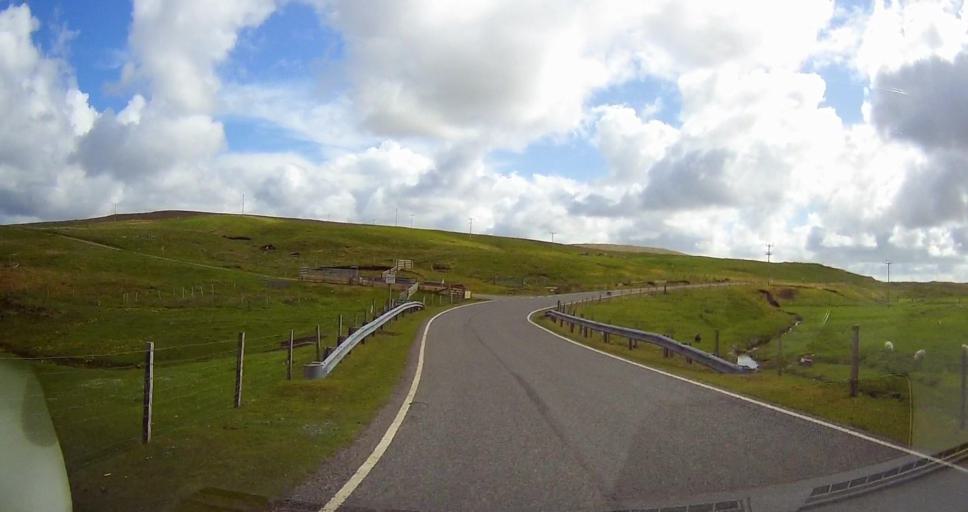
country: GB
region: Scotland
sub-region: Shetland Islands
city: Lerwick
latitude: 60.5256
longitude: -1.3718
